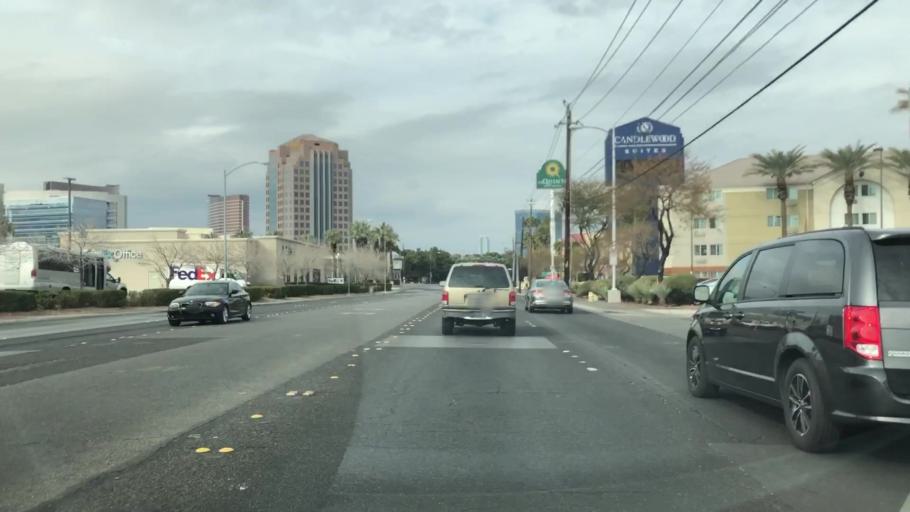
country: US
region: Nevada
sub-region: Clark County
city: Paradise
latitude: 36.1153
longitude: -115.1542
